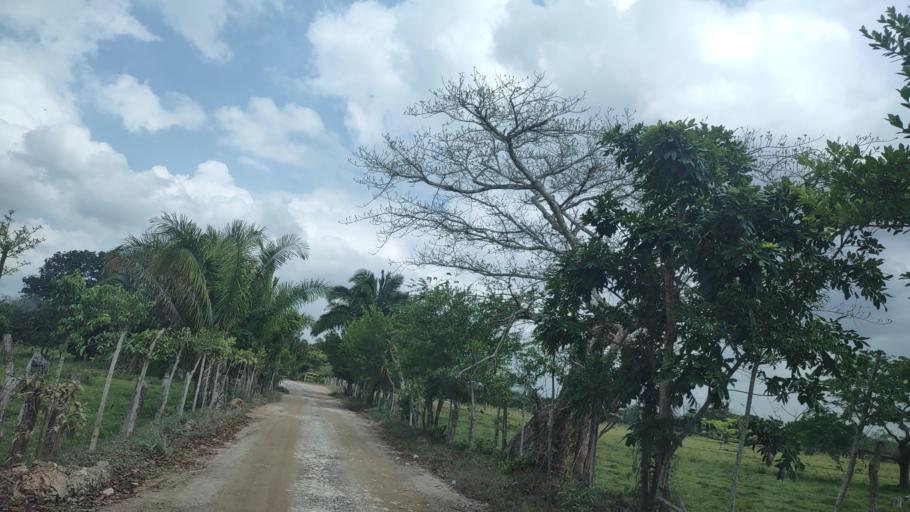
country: MX
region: Veracruz
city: Las Choapas
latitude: 17.9613
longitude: -94.1215
